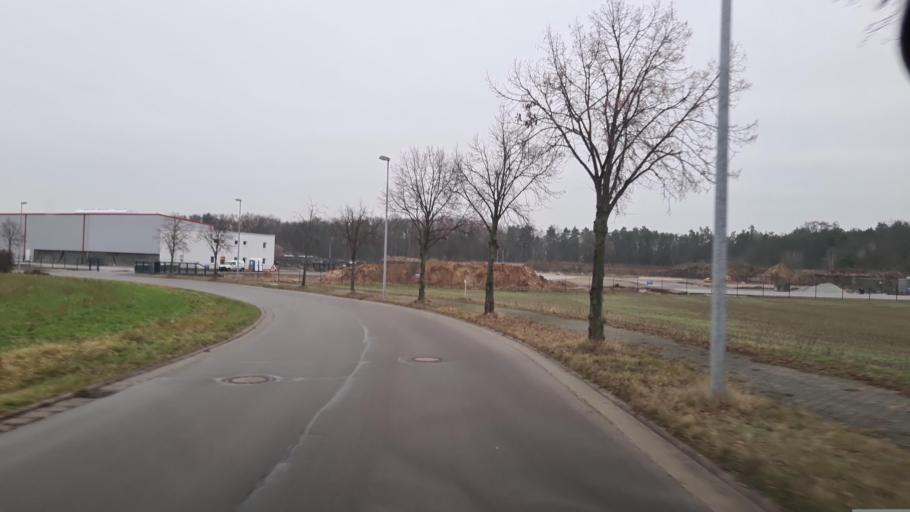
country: DE
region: Brandenburg
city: Werben
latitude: 51.7644
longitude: 14.1631
